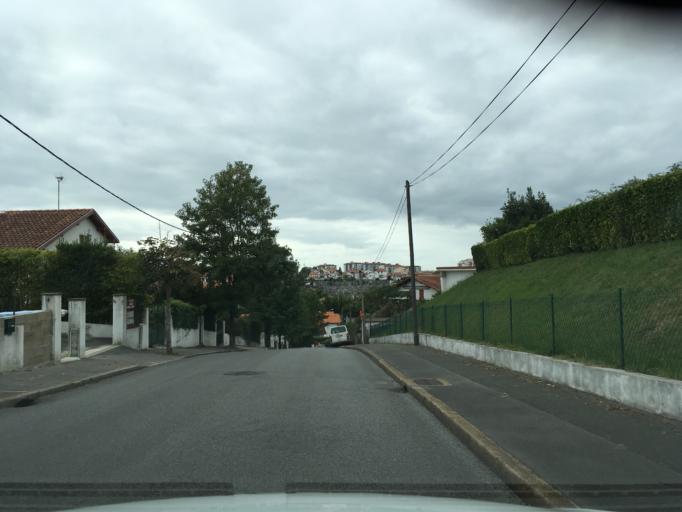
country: FR
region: Aquitaine
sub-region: Departement des Pyrenees-Atlantiques
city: Biarritz
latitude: 43.4736
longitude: -1.5425
